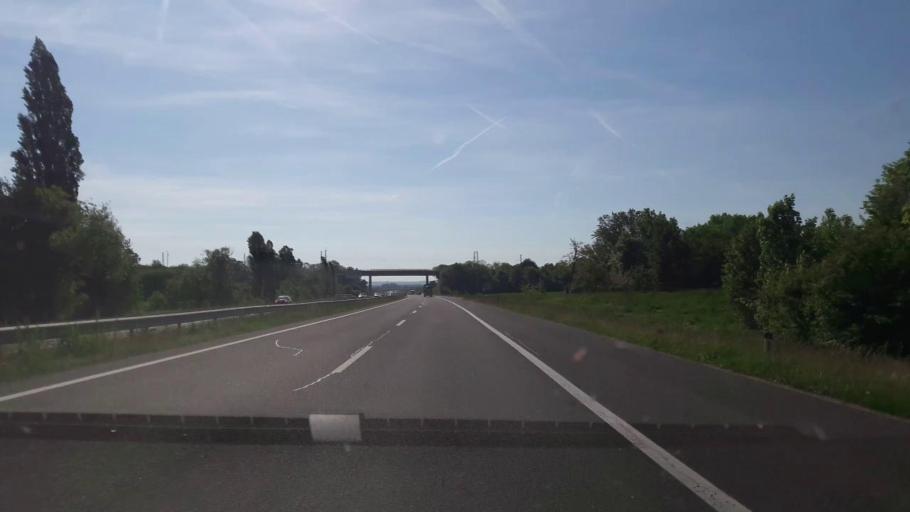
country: AT
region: Burgenland
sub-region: Eisenstadt-Umgebung
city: Mullendorf
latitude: 47.8318
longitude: 16.4568
